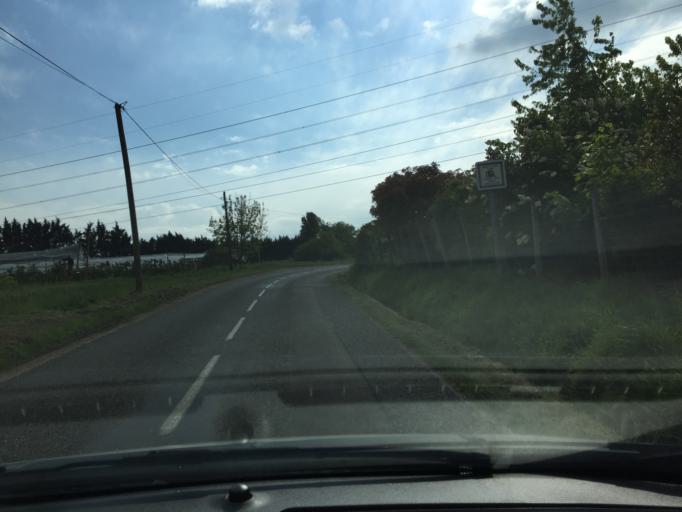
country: FR
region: Rhone-Alpes
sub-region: Departement du Rhone
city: Orlienas
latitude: 45.6454
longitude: 4.6961
